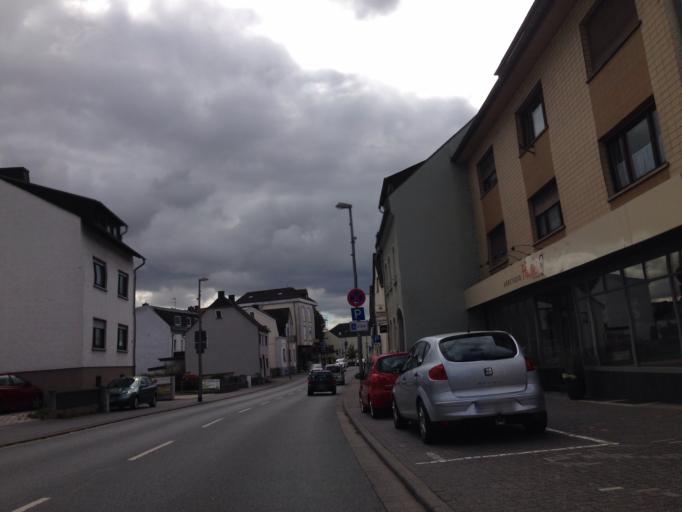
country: DE
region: Hesse
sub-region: Regierungsbezirk Giessen
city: Elz
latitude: 50.4126
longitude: 8.0360
